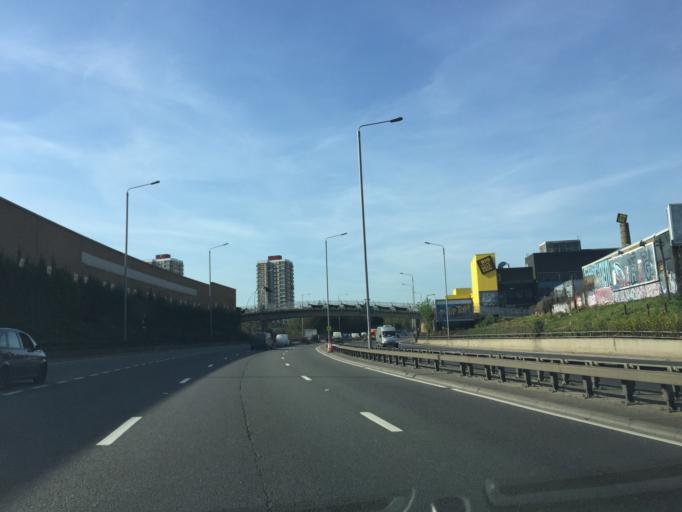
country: GB
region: England
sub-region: Greater London
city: Poplar
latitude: 51.5350
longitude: -0.0244
